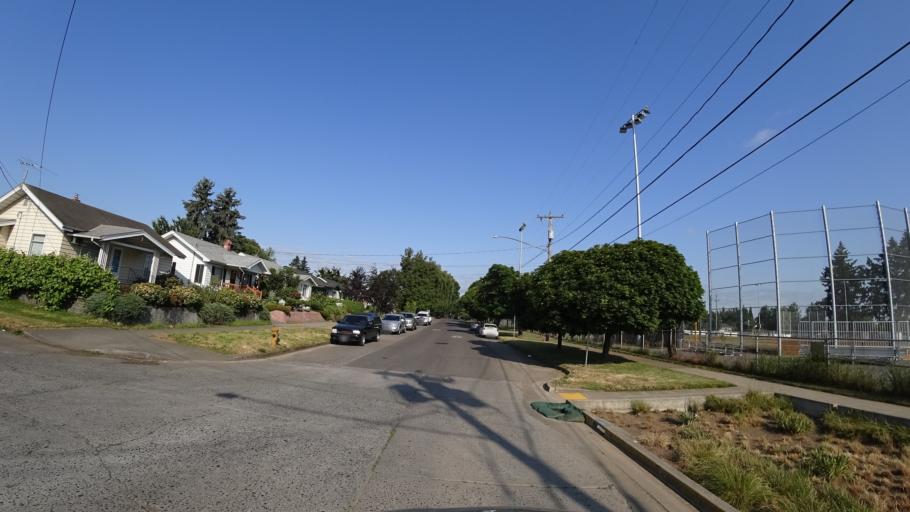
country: US
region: Oregon
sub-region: Washington County
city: West Haven
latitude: 45.5886
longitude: -122.7395
